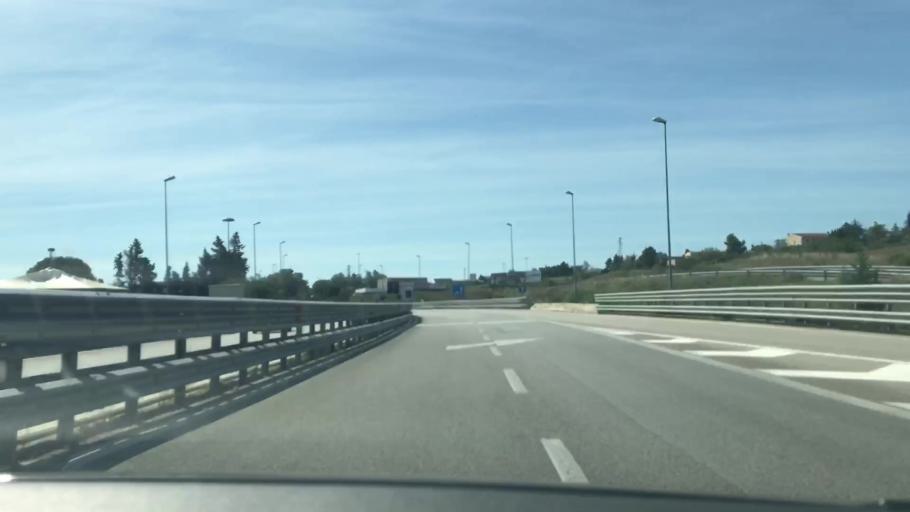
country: IT
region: Basilicate
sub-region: Provincia di Matera
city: Matera
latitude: 40.6898
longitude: 16.5905
